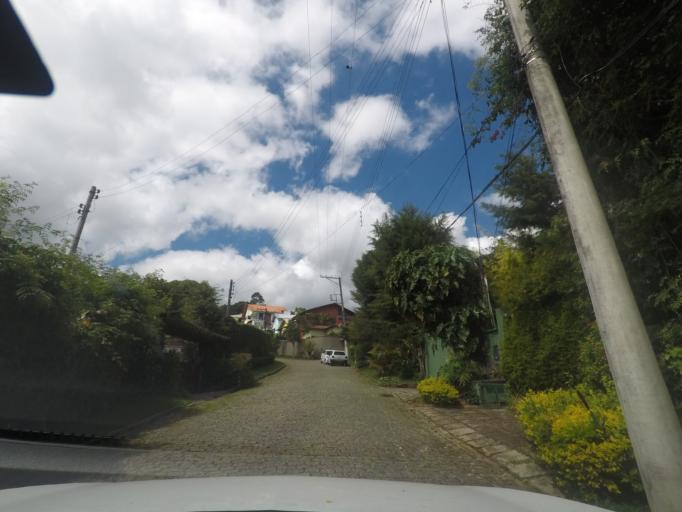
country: BR
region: Rio de Janeiro
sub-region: Teresopolis
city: Teresopolis
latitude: -22.3955
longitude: -42.9882
